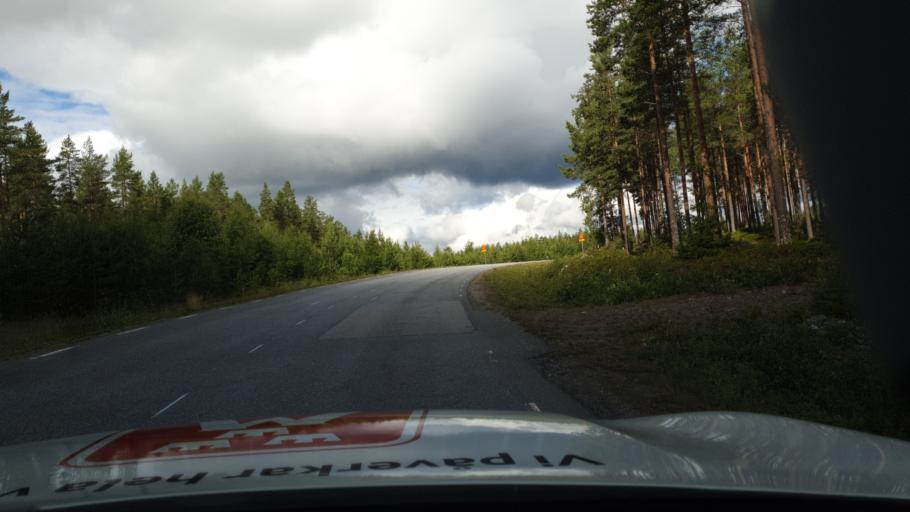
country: SE
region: Vaesterbotten
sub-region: Umea Kommun
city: Hoernefors
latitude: 63.6794
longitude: 20.0250
